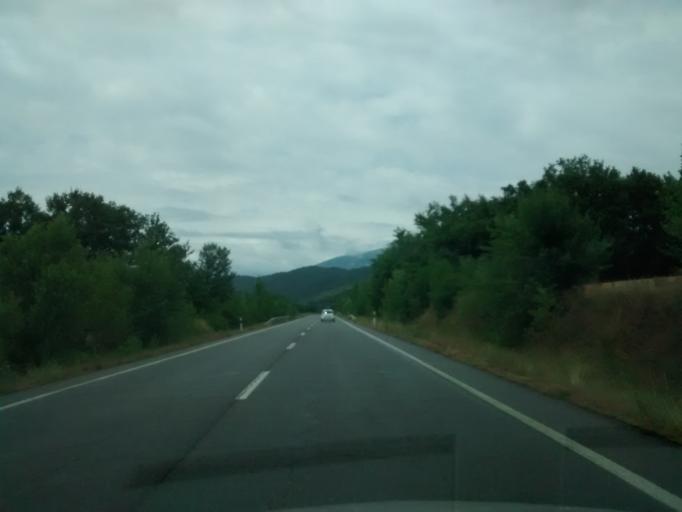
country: ES
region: Aragon
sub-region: Provincia de Huesca
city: Ainsa
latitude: 42.4256
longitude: 0.1213
